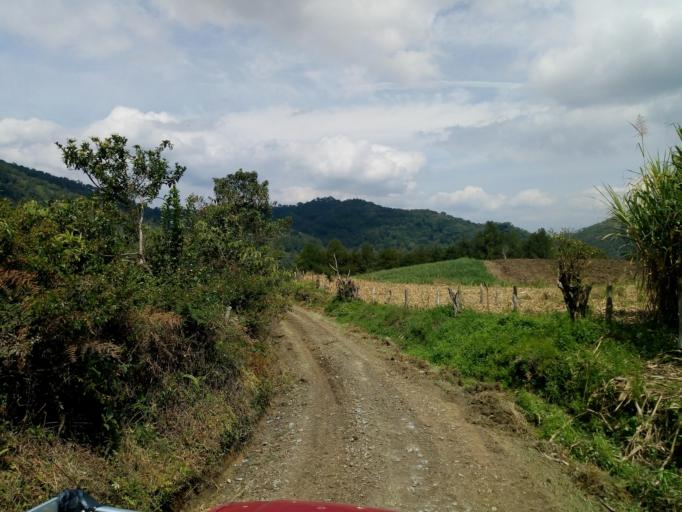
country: CO
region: Boyaca
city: Moniquira
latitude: 5.8651
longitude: -73.5257
